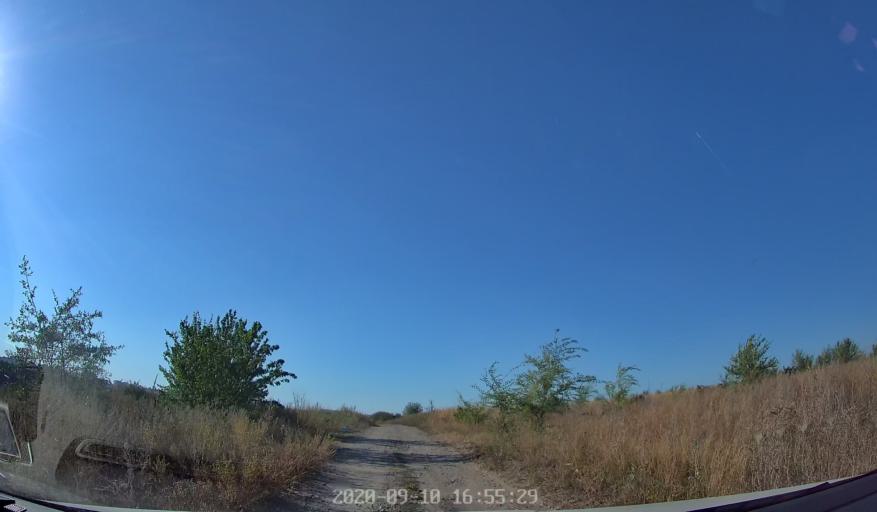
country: MD
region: Chisinau
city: Stauceni
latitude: 47.0543
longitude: 28.9193
